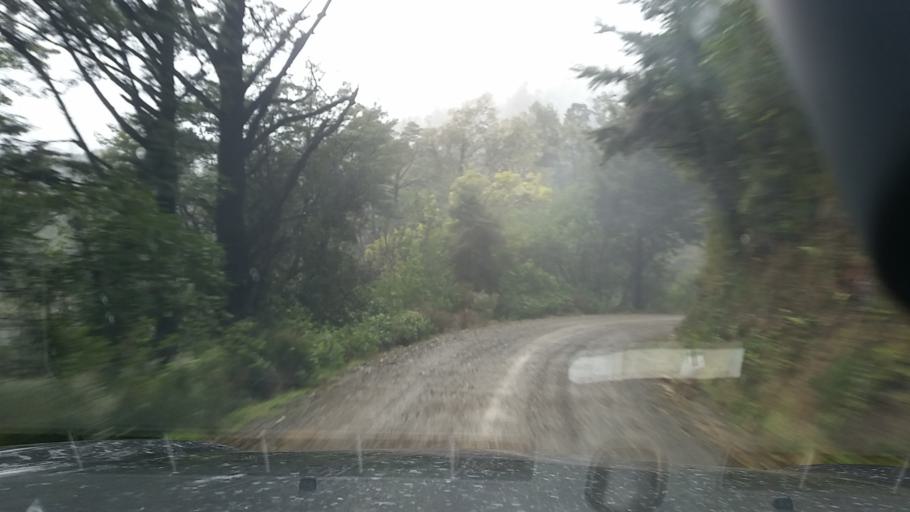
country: NZ
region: Nelson
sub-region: Nelson City
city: Nelson
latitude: -41.3709
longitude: 173.6057
